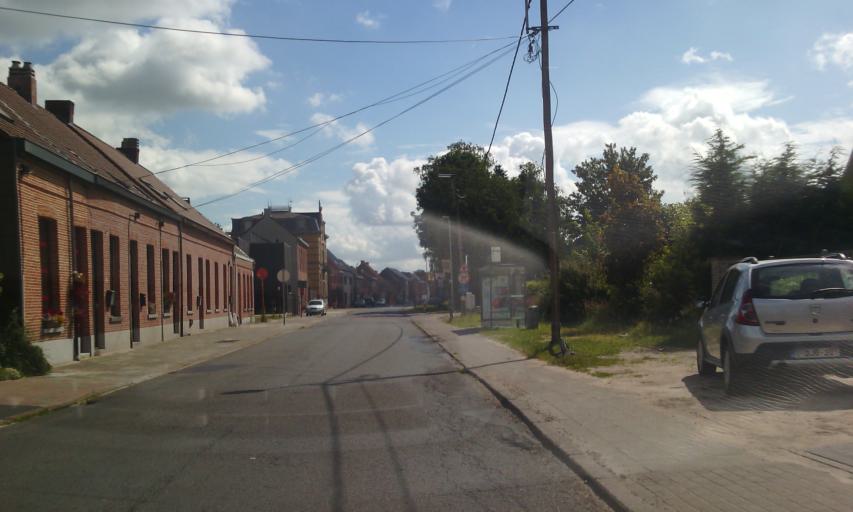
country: BE
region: Flanders
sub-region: Provincie Oost-Vlaanderen
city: Stekene
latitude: 51.1574
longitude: 4.0326
